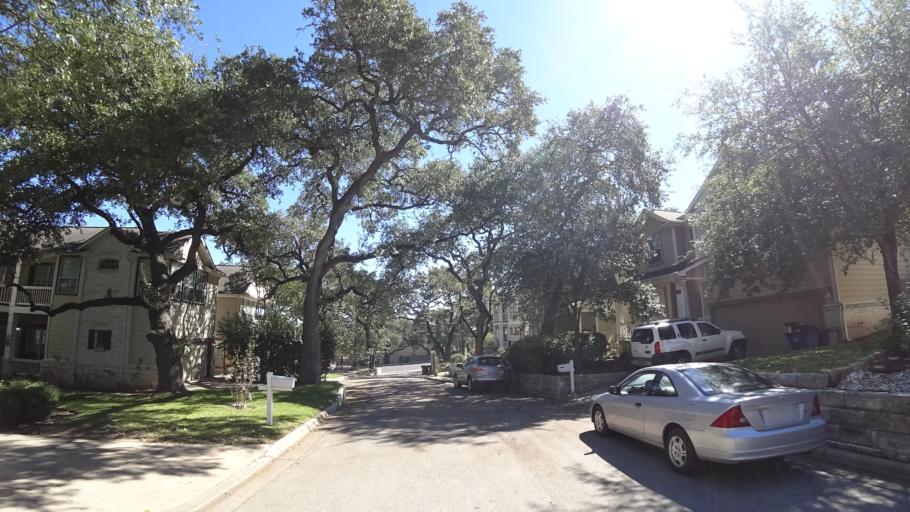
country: US
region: Texas
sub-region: Travis County
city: Austin
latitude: 30.2339
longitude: -97.7656
